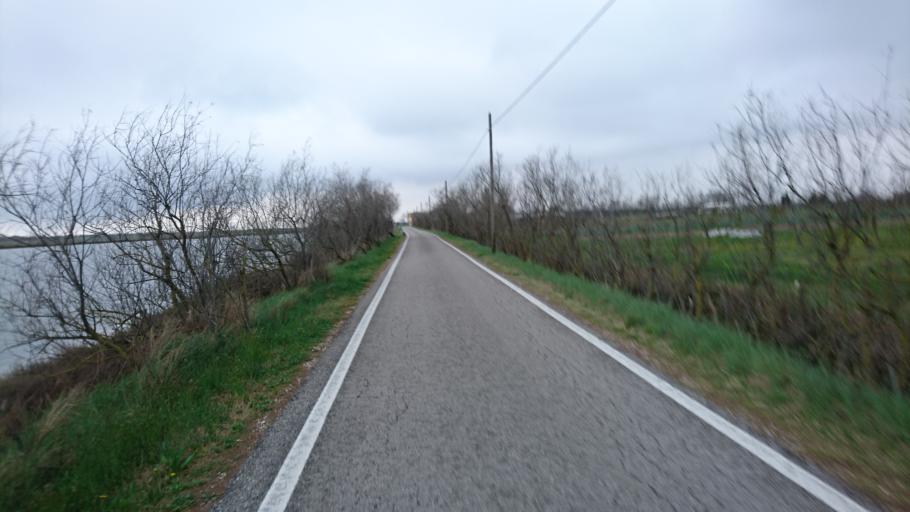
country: IT
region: Veneto
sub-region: Provincia di Venezia
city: Ca' Savio
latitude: 45.4903
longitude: 12.4948
